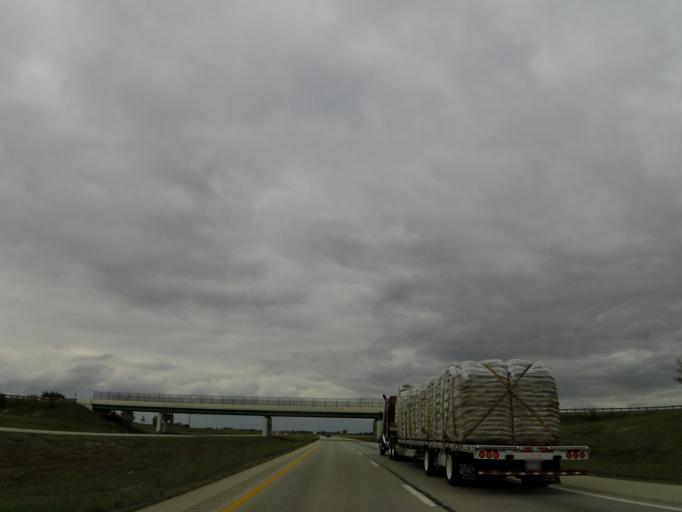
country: US
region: Ohio
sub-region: Greene County
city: Jamestown
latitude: 39.5566
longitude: -83.7204
